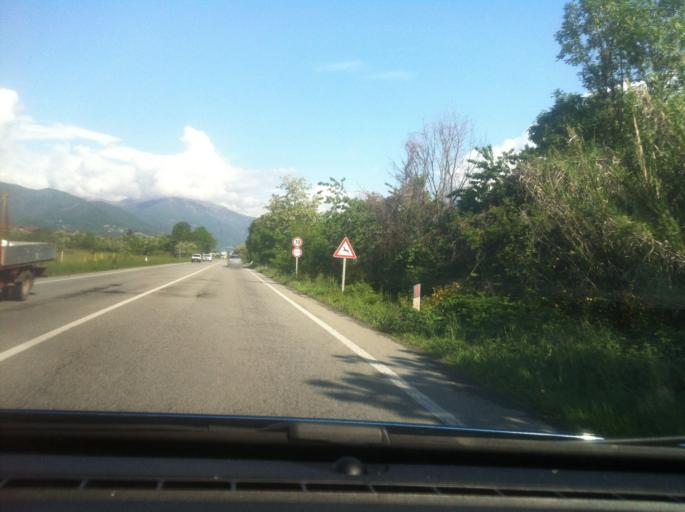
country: IT
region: Piedmont
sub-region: Provincia di Torino
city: Salassa
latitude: 45.3618
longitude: 7.6891
